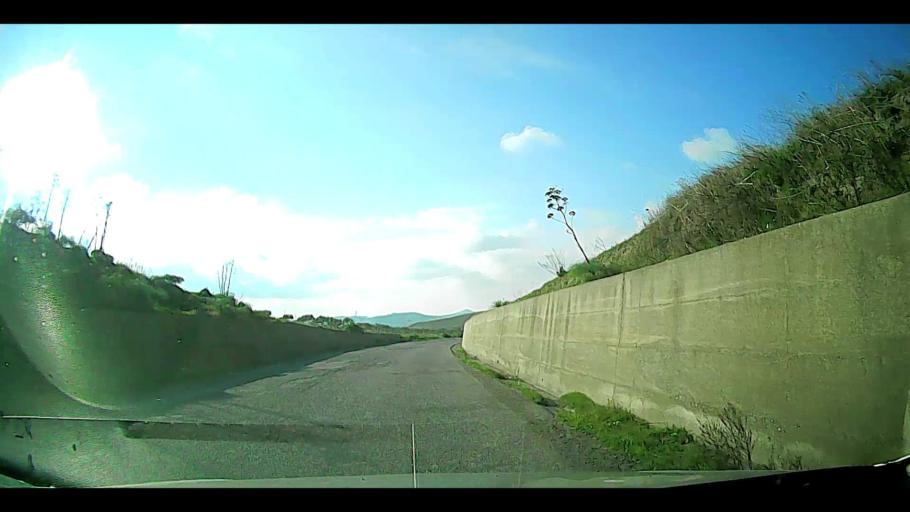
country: IT
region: Calabria
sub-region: Provincia di Crotone
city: Rocca di Neto
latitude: 39.1914
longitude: 17.0584
